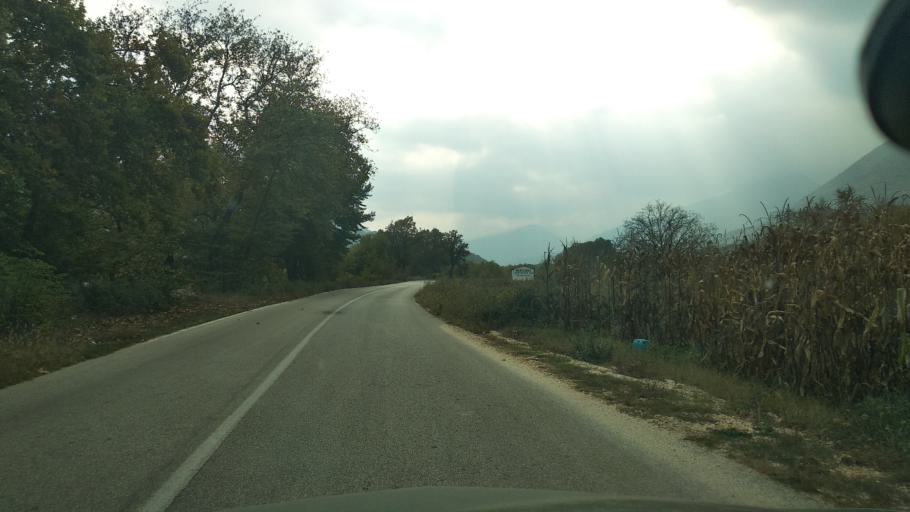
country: GR
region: Thessaly
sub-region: Trikala
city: Kastraki
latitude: 39.7029
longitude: 21.5262
